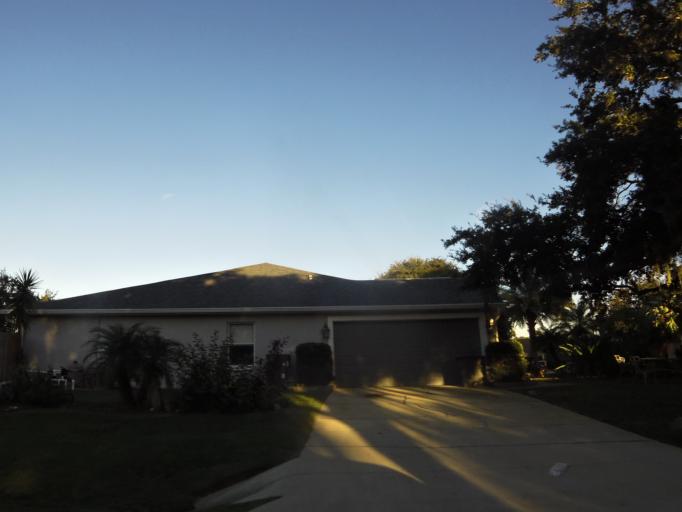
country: US
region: Florida
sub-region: Flagler County
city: Palm Coast
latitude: 29.5625
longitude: -81.2056
